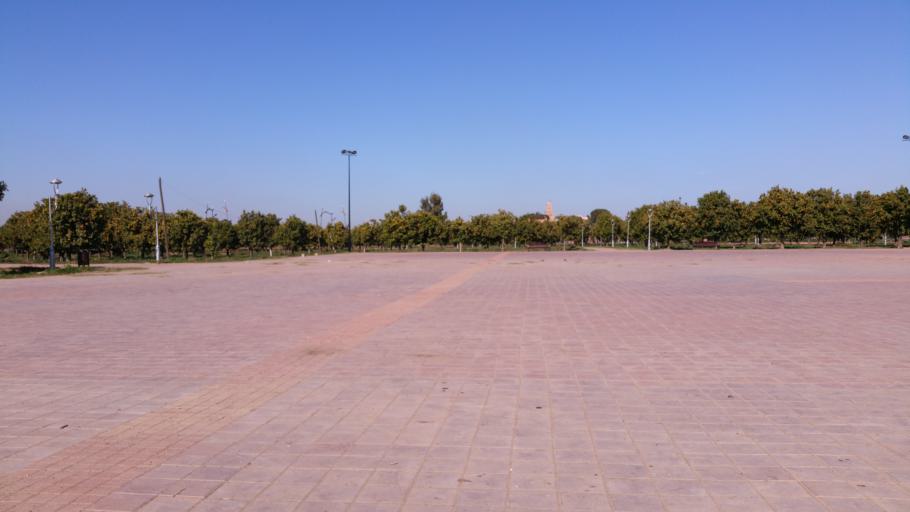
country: MA
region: Marrakech-Tensift-Al Haouz
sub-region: Marrakech
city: Marrakesh
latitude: 31.6135
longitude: -7.9914
